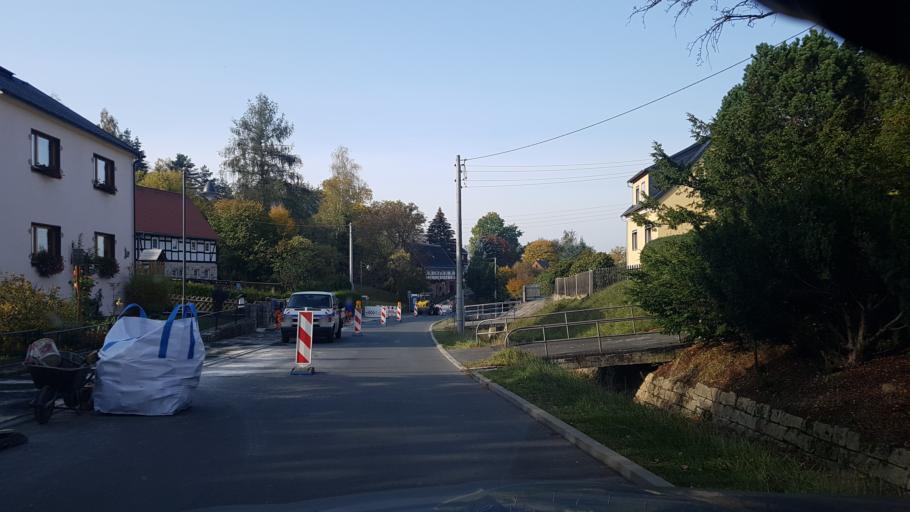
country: DE
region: Saxony
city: Konigstein
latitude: 50.9106
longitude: 14.0756
